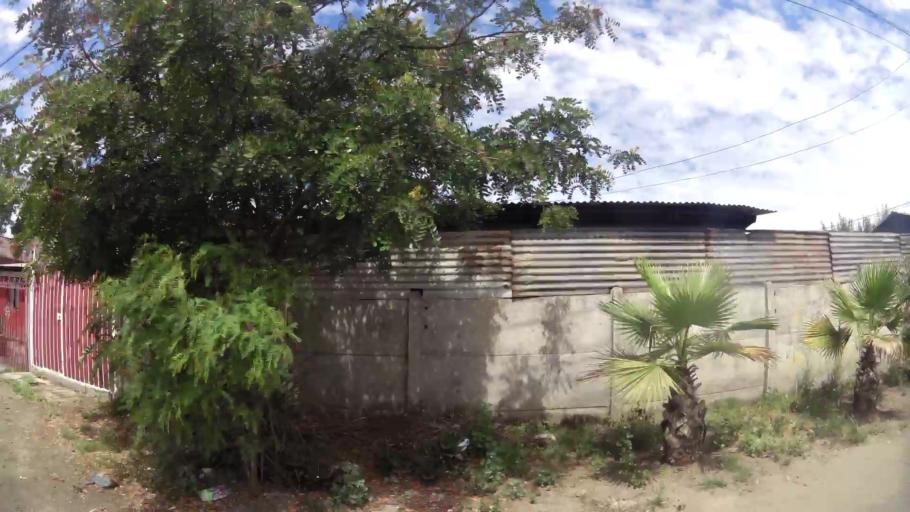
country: CL
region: Santiago Metropolitan
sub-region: Provincia de Santiago
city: La Pintana
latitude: -33.5737
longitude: -70.6593
